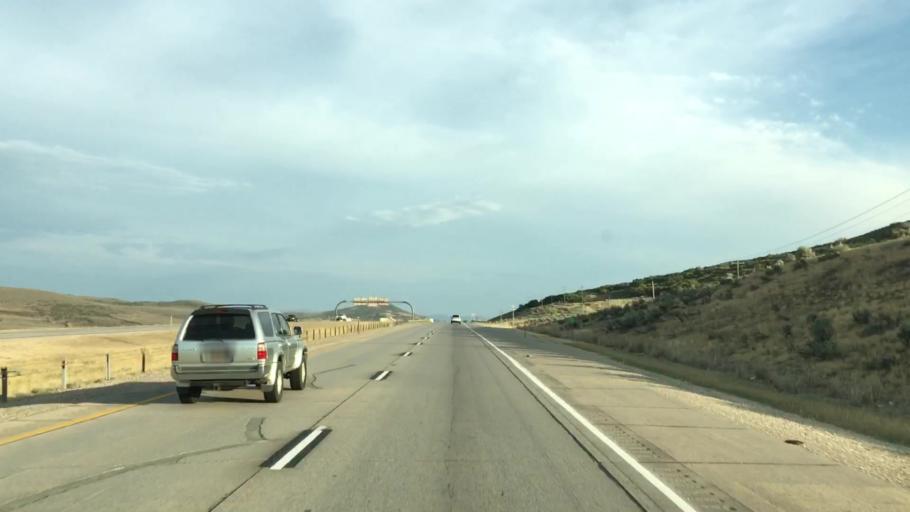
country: US
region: Utah
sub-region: Summit County
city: Snyderville
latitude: 40.7093
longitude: -111.4816
